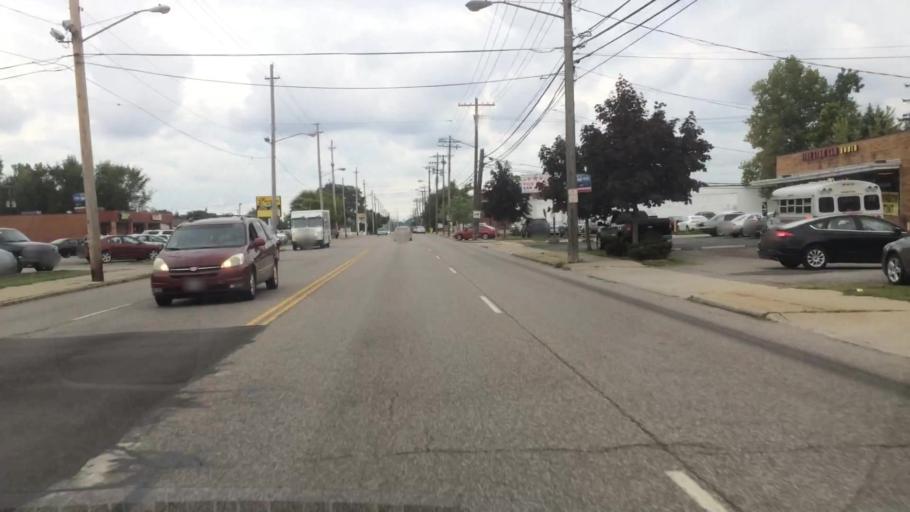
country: US
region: Ohio
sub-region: Cuyahoga County
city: Maple Heights
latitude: 41.4082
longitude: -81.5601
